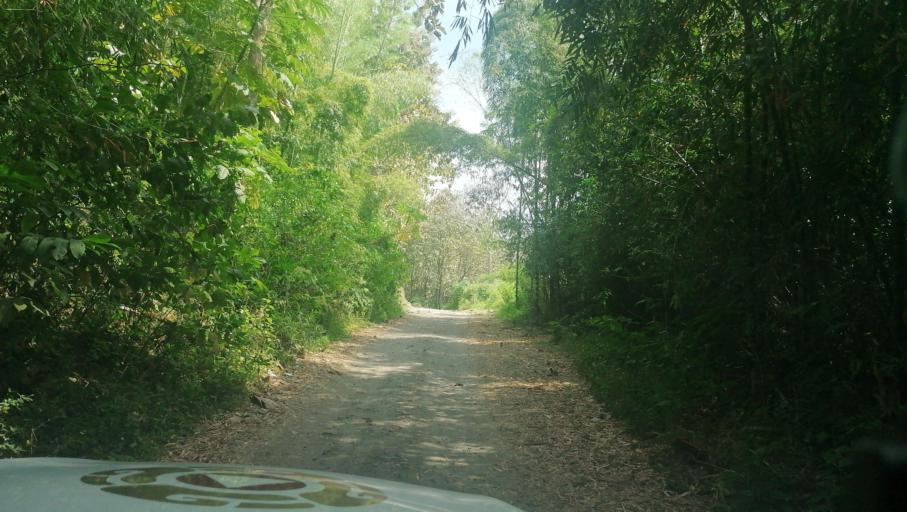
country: MX
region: Chiapas
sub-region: Cacahoatan
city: Benito Juarez
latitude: 15.0310
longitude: -92.2350
